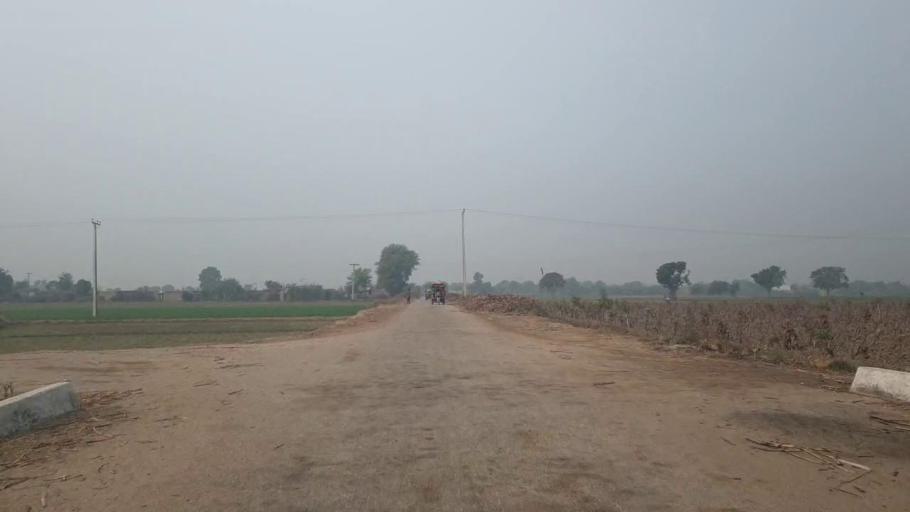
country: PK
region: Sindh
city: Tando Adam
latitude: 25.7098
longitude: 68.6525
